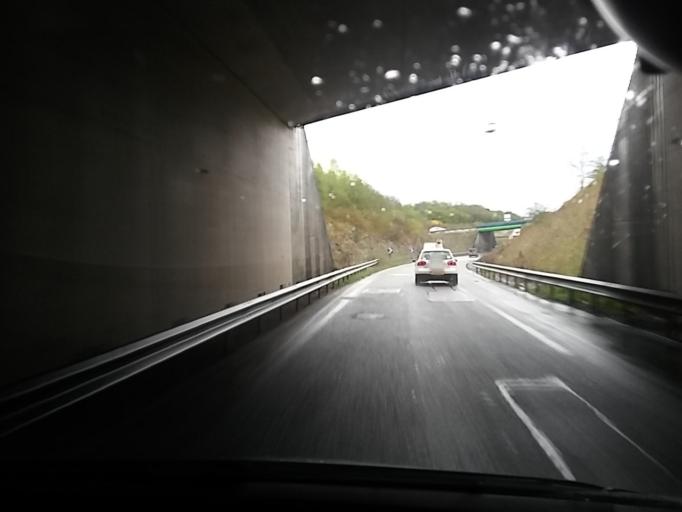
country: FR
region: Picardie
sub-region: Departement de la Somme
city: Longueau
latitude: 49.8638
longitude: 2.3748
